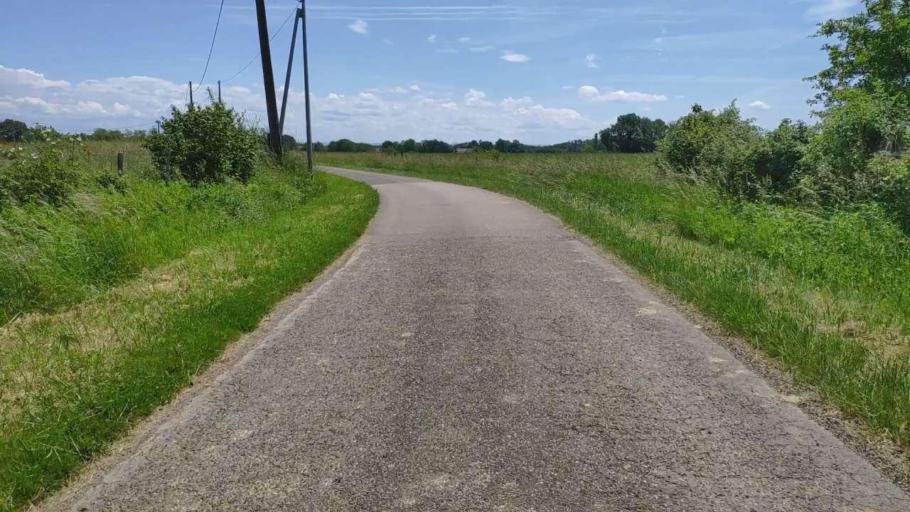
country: FR
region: Franche-Comte
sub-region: Departement du Jura
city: Bletterans
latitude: 46.7915
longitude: 5.3713
